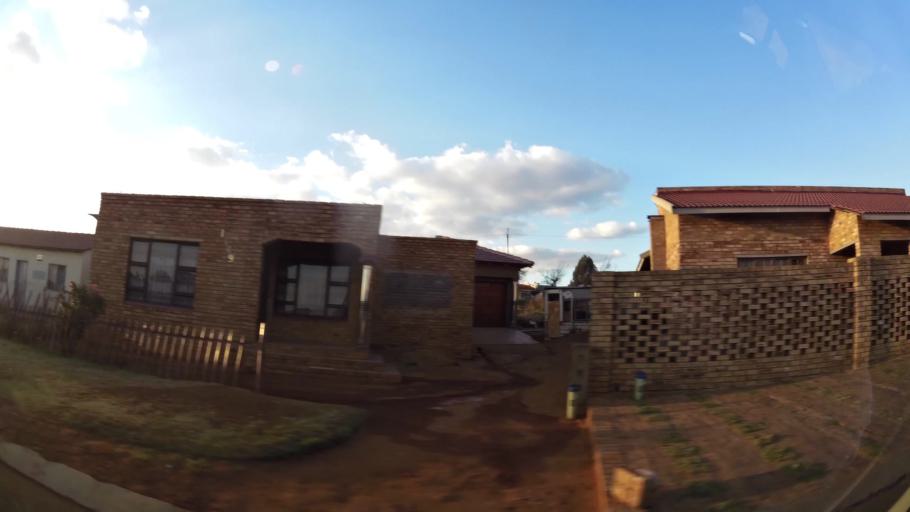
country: ZA
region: Gauteng
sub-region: West Rand District Municipality
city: Krugersdorp
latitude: -26.0769
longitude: 27.7556
